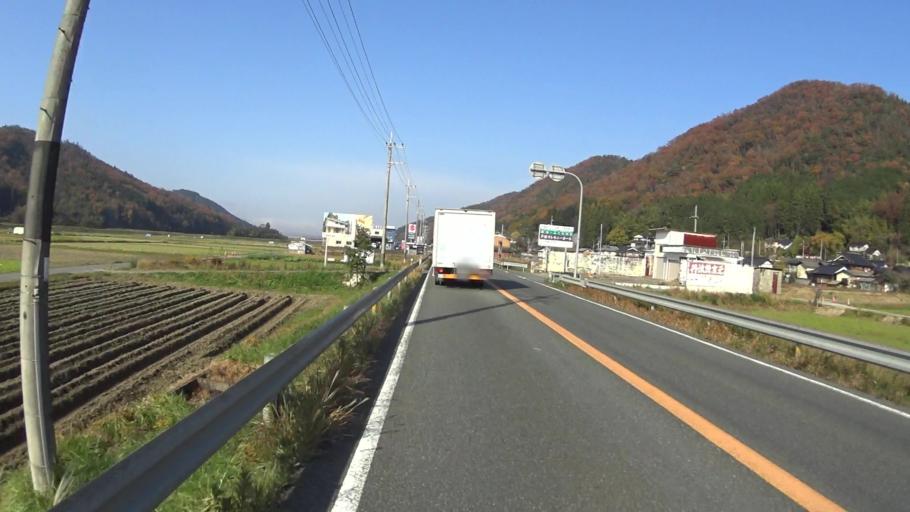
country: JP
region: Kyoto
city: Ayabe
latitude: 35.2530
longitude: 135.2066
